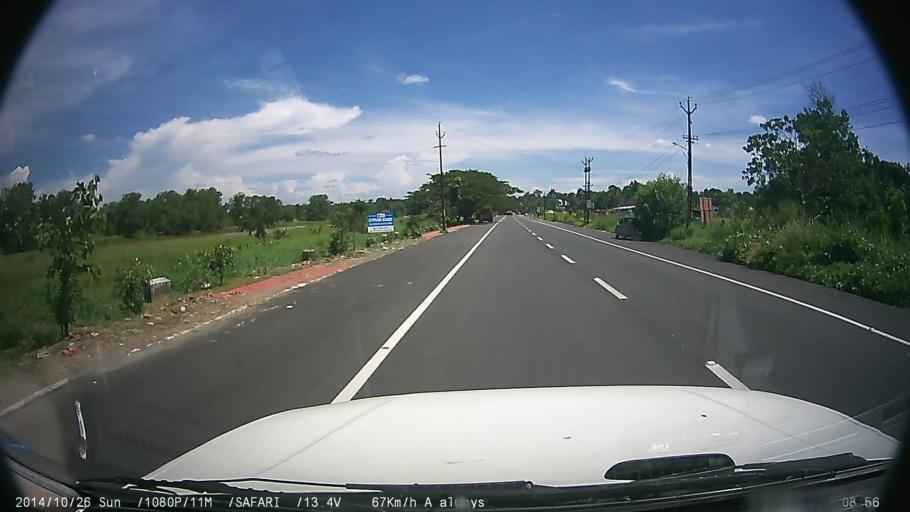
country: IN
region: Kerala
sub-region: Kottayam
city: Changanacheri
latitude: 9.4631
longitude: 76.5338
